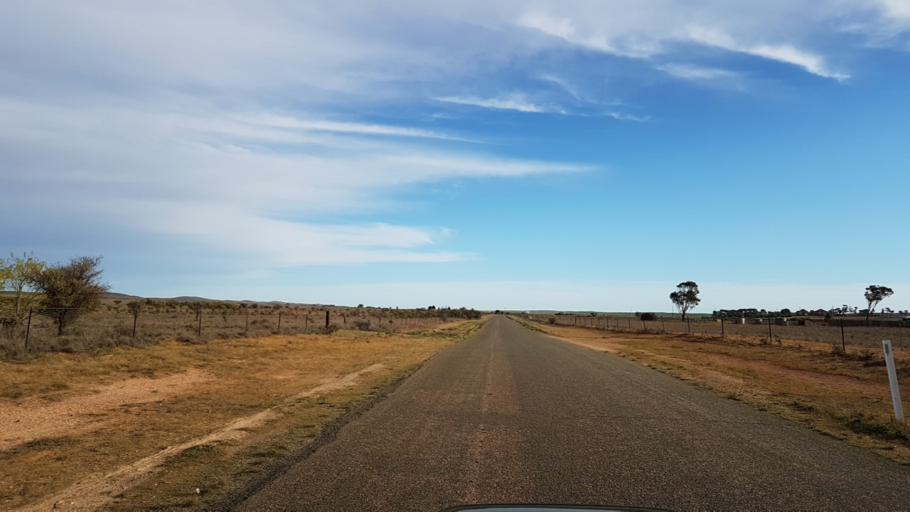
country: AU
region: South Australia
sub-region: Peterborough
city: Peterborough
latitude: -32.9855
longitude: 138.8505
